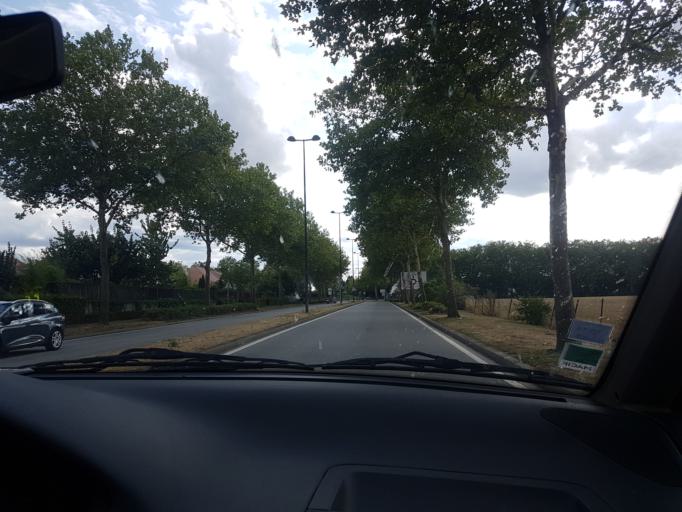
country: FR
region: Ile-de-France
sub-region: Departement des Yvelines
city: Elancourt
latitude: 48.7950
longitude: 1.9631
